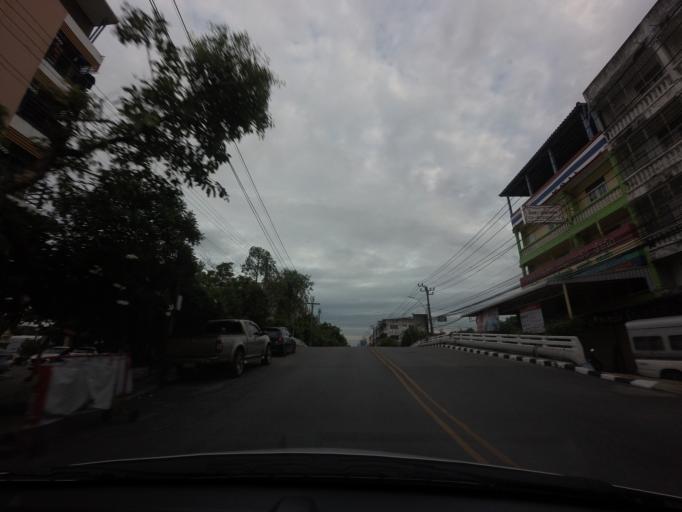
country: TH
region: Bangkok
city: Chom Thong
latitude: 13.6859
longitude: 100.4636
